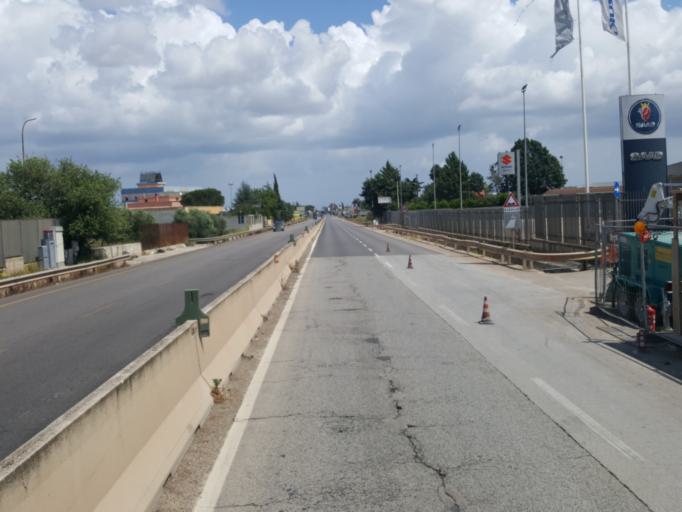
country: IT
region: Apulia
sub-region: Provincia di Bari
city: Bitetto
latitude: 41.0763
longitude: 16.7566
